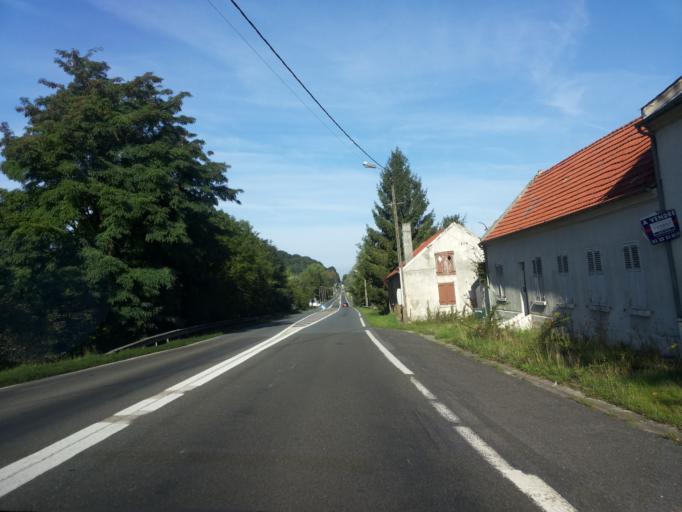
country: FR
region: Picardie
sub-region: Departement de l'Aisne
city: Crepy
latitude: 49.6132
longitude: 3.4738
